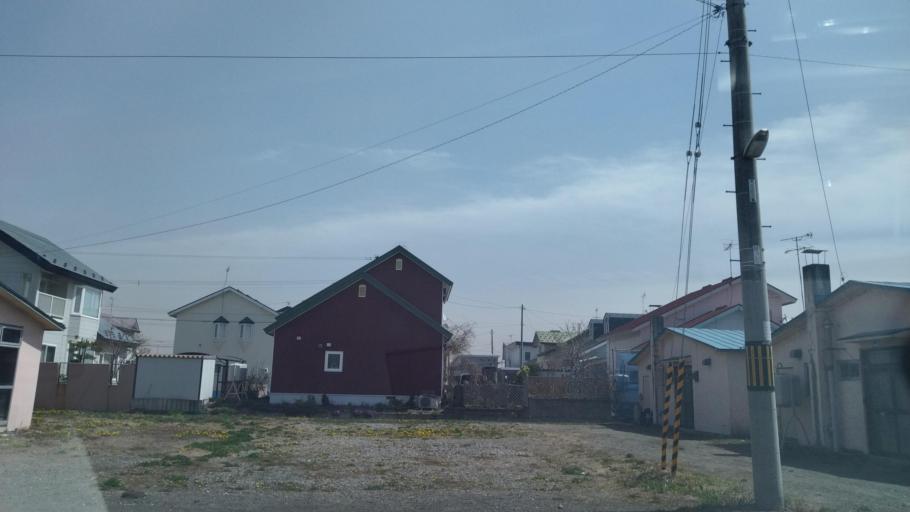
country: JP
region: Hokkaido
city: Obihiro
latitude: 42.9347
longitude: 143.1865
